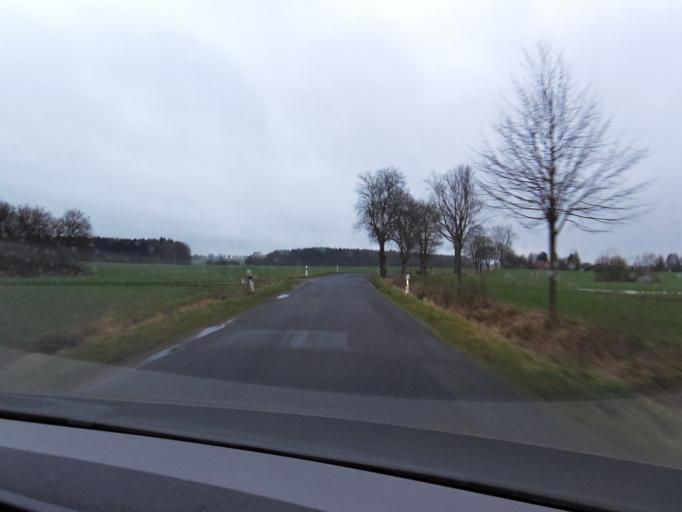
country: DE
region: Mecklenburg-Vorpommern
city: Roggendorf
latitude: 53.7083
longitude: 11.0310
